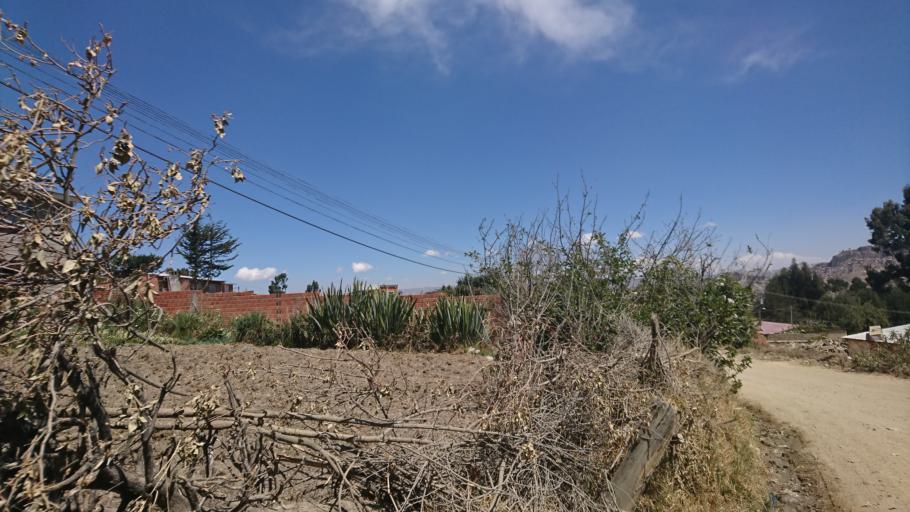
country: BO
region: La Paz
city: La Paz
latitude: -16.4894
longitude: -68.0801
